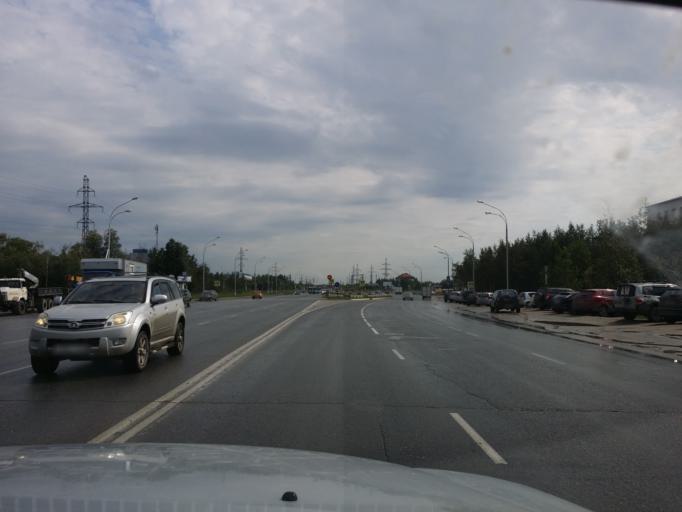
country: RU
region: Khanty-Mansiyskiy Avtonomnyy Okrug
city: Nizhnevartovsk
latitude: 60.9418
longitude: 76.5301
